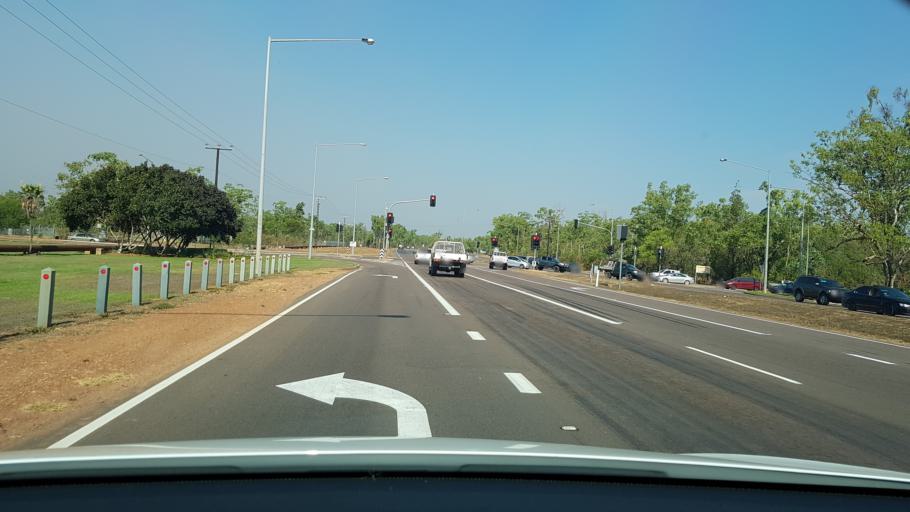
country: AU
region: Northern Territory
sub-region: Litchfield
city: Virginia
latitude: -12.5243
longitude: 131.0437
